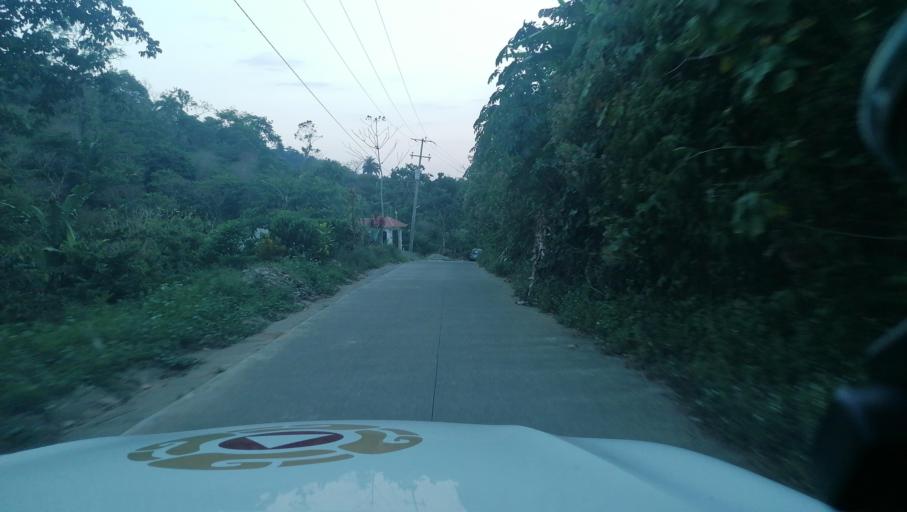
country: MX
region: Chiapas
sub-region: Cacahoatan
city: Benito Juarez
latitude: 15.0530
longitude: -92.2427
